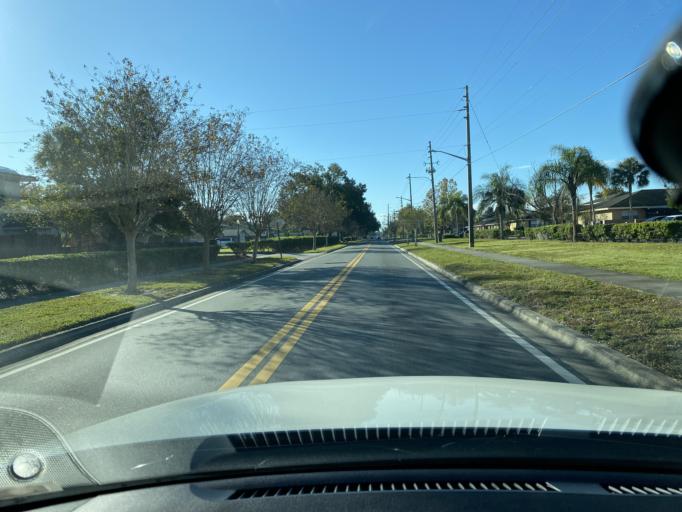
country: US
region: Florida
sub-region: Orange County
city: Azalea Park
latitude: 28.5240
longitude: -81.3022
